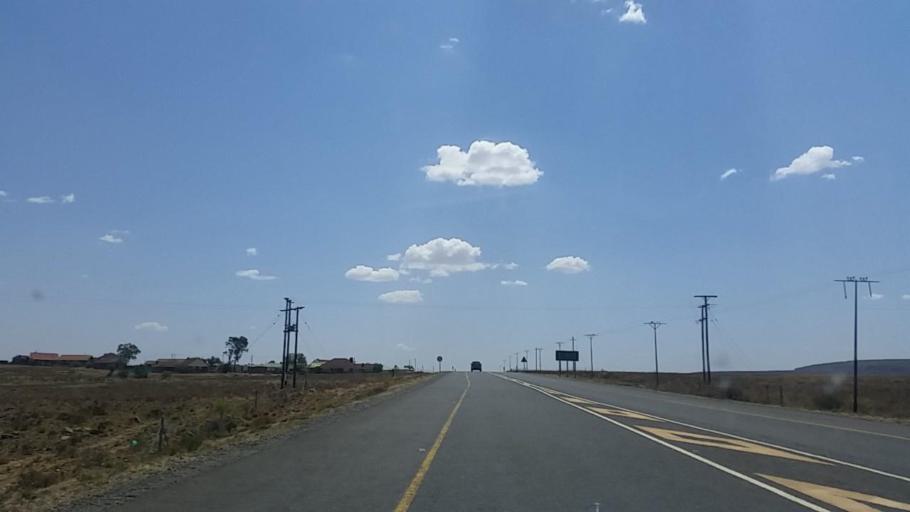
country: ZA
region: Northern Cape
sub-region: Pixley ka Seme District Municipality
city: Noupoort
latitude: -31.1851
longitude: 24.9634
